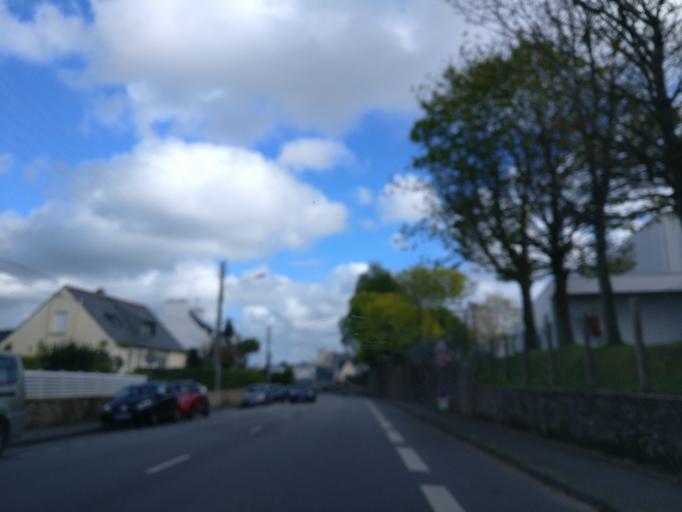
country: FR
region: Brittany
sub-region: Departement du Finistere
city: Brest
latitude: 48.4031
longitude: -4.4576
